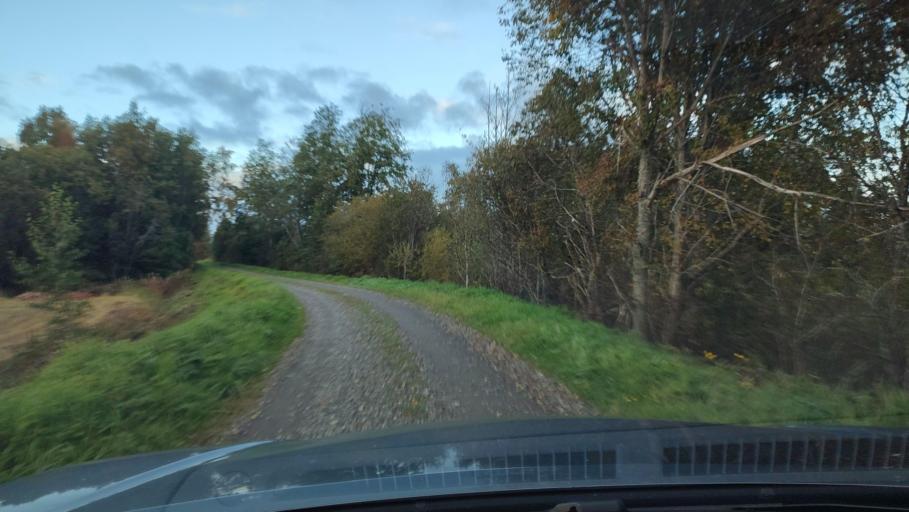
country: FI
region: Ostrobothnia
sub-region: Sydosterbotten
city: Kristinestad
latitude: 62.2347
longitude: 21.4514
